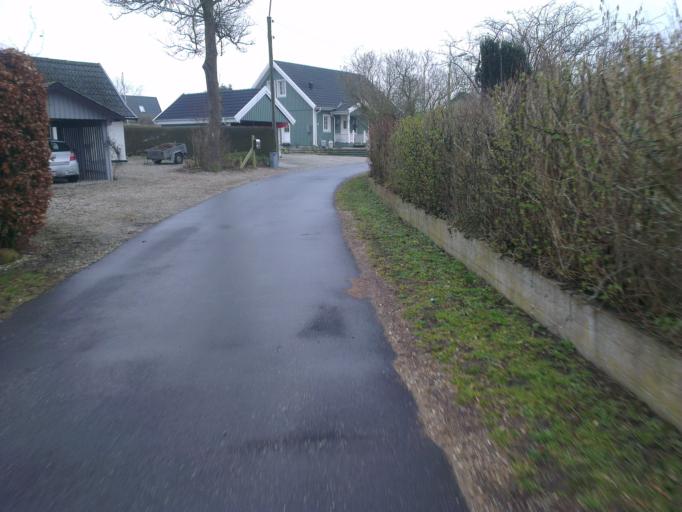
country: DK
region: Capital Region
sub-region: Frederikssund Kommune
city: Skibby
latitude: 55.7936
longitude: 11.9168
